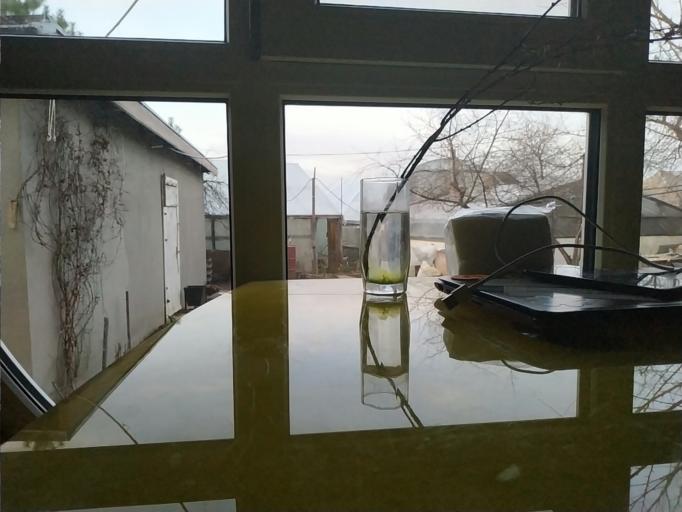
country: RU
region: Republic of Karelia
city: Suoyarvi
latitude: 62.4668
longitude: 31.9963
